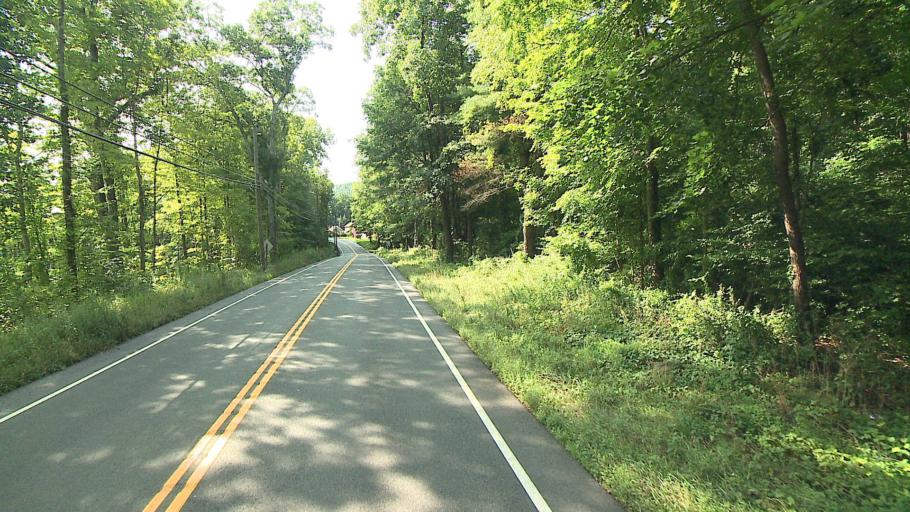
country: US
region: Connecticut
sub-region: Fairfield County
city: Sherman
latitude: 41.6024
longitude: -73.4592
